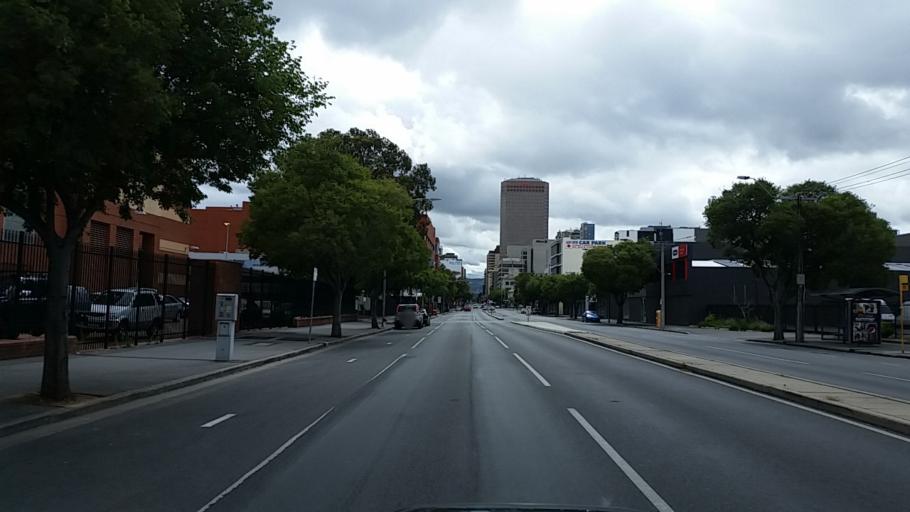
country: AU
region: South Australia
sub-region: Adelaide
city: Adelaide
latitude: -34.9248
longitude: 138.5902
